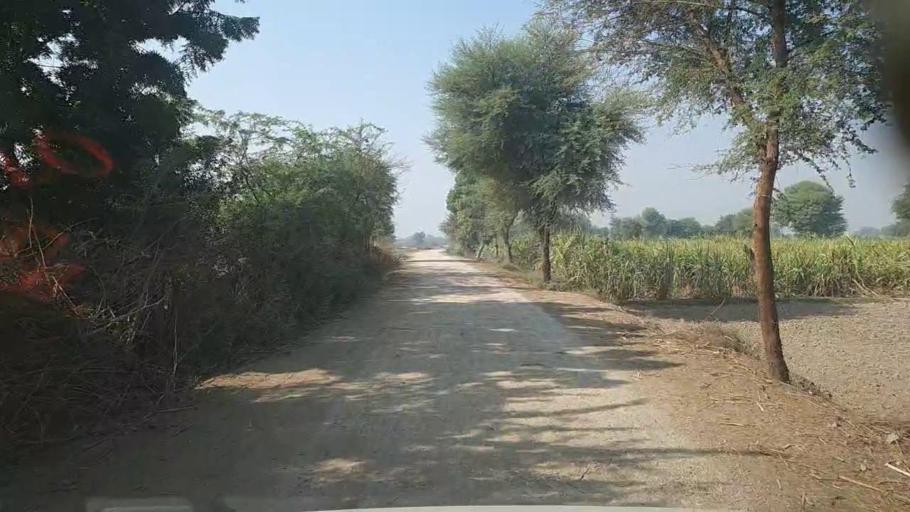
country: PK
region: Sindh
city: Kandiari
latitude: 26.9723
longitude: 68.4545
